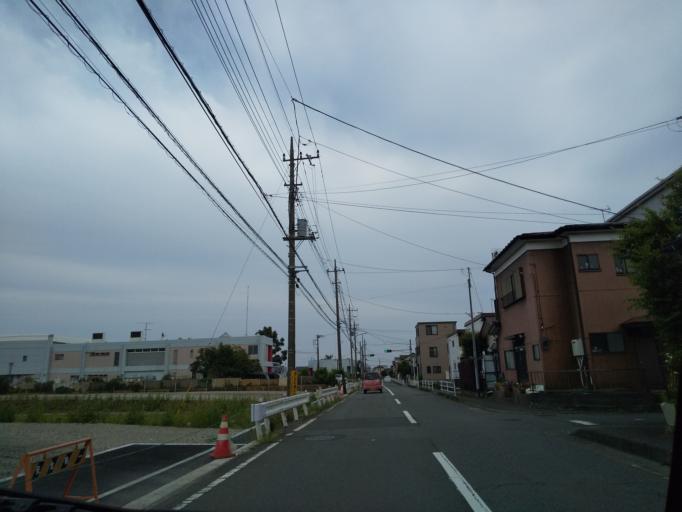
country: JP
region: Kanagawa
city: Atsugi
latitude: 35.4719
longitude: 139.3547
